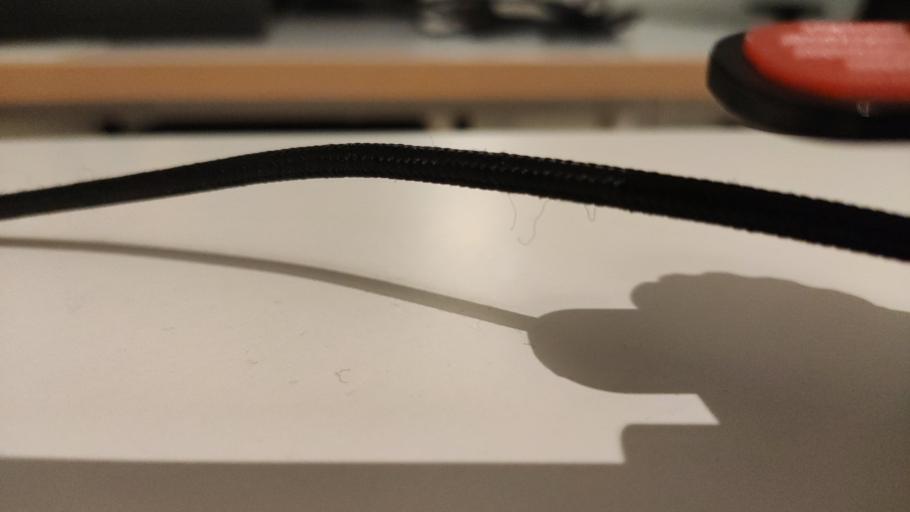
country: RU
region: Moskovskaya
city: Novosin'kovo
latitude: 56.3716
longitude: 37.3455
